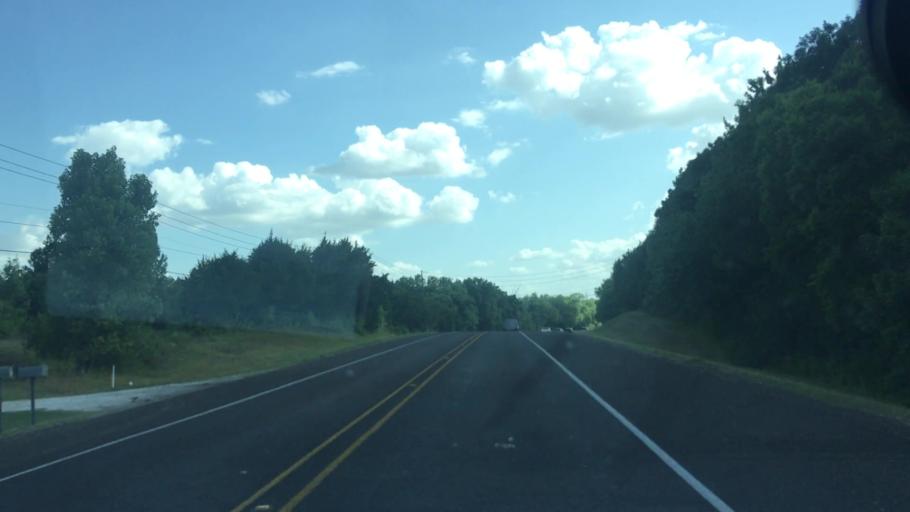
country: US
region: Texas
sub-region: Dallas County
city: Lancaster
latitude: 32.5699
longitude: -96.7616
